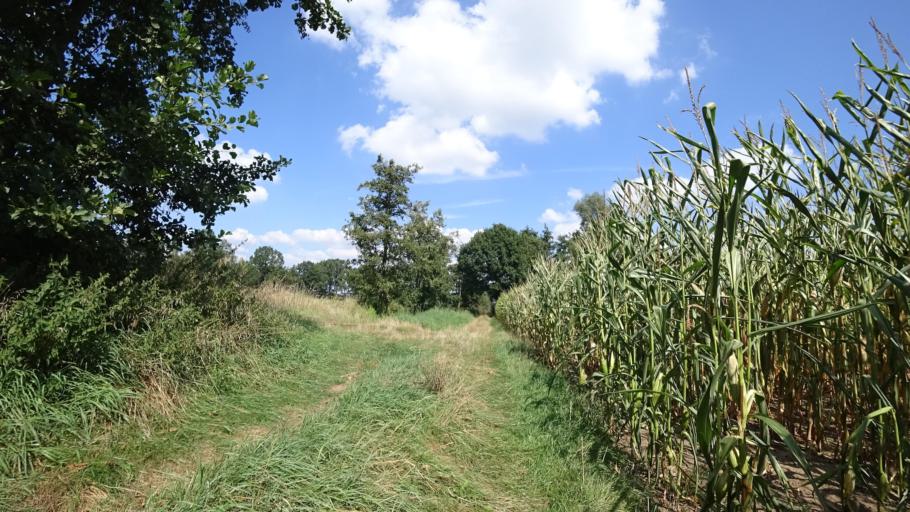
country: DE
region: North Rhine-Westphalia
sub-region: Regierungsbezirk Detmold
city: Rheda-Wiedenbruck
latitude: 51.8831
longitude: 8.3020
